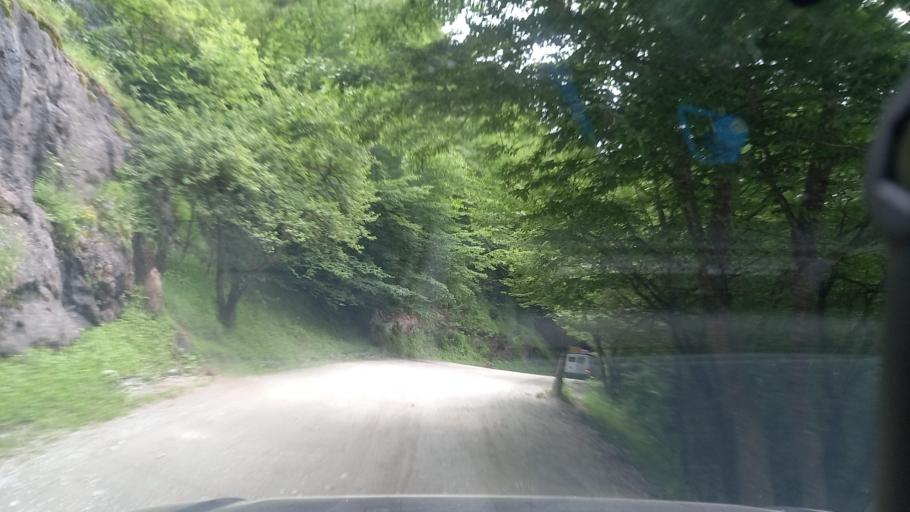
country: RU
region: Karachayevo-Cherkesiya
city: Kurdzhinovo
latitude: 43.8209
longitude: 40.9159
